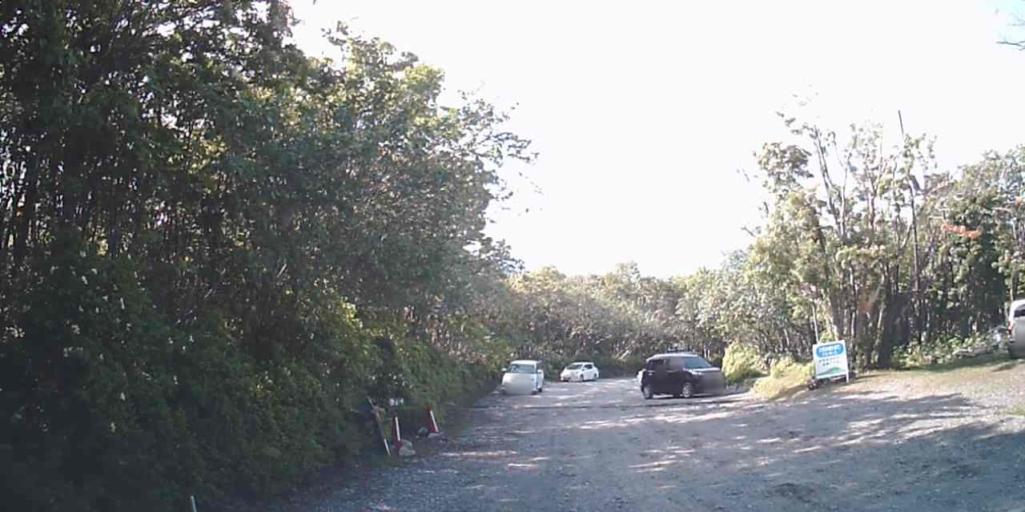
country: JP
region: Hokkaido
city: Shiraoi
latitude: 42.6992
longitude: 141.3900
